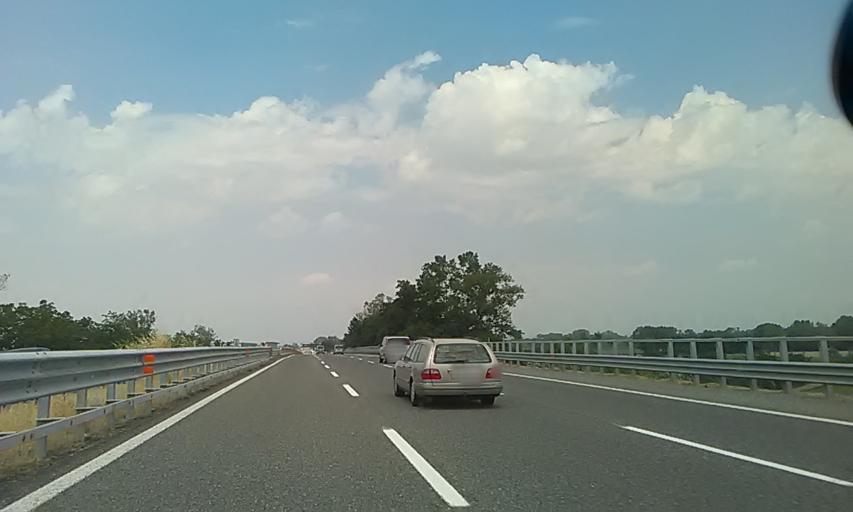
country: IT
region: Piedmont
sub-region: Provincia di Alessandria
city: Castellazzo Bormida
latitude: 44.8502
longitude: 8.5919
